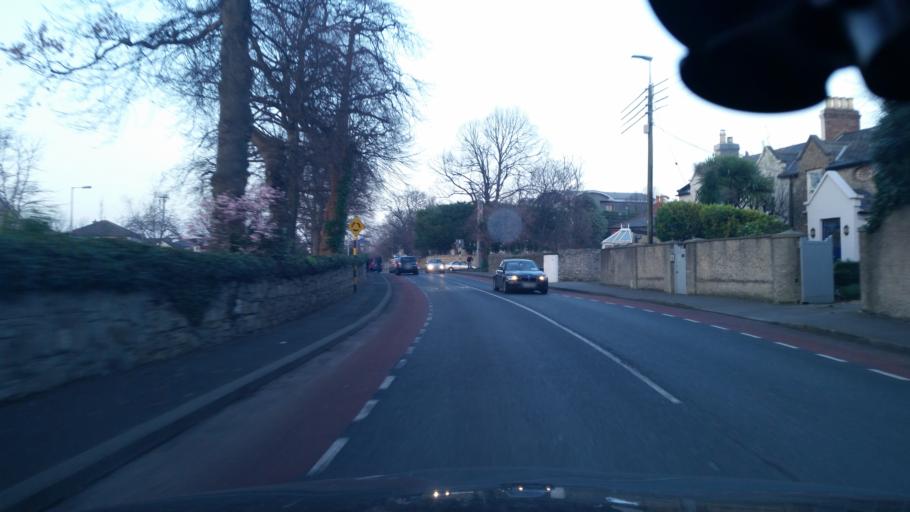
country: IE
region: Leinster
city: Shankill
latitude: 53.2279
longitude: -6.1246
